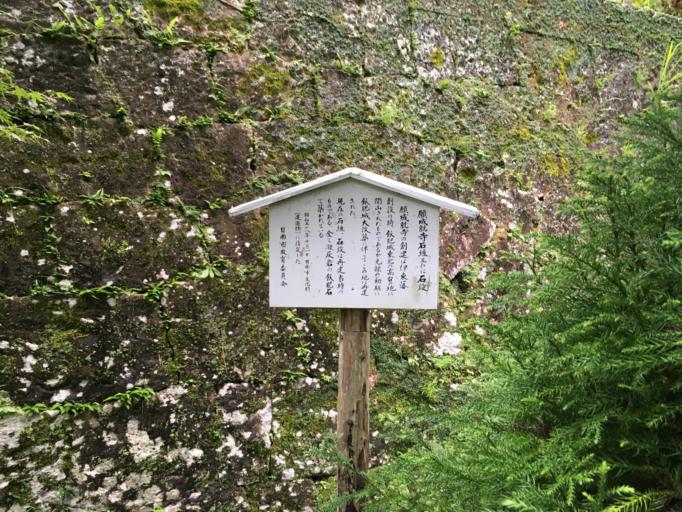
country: JP
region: Miyazaki
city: Nichinan
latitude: 31.6301
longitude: 131.3596
